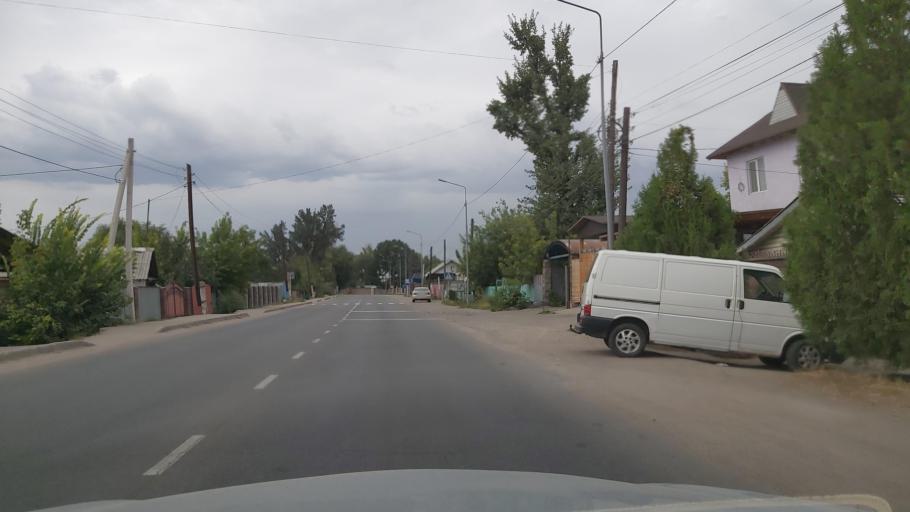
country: KZ
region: Almaty Oblysy
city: Energeticheskiy
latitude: 43.3849
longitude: 77.0784
